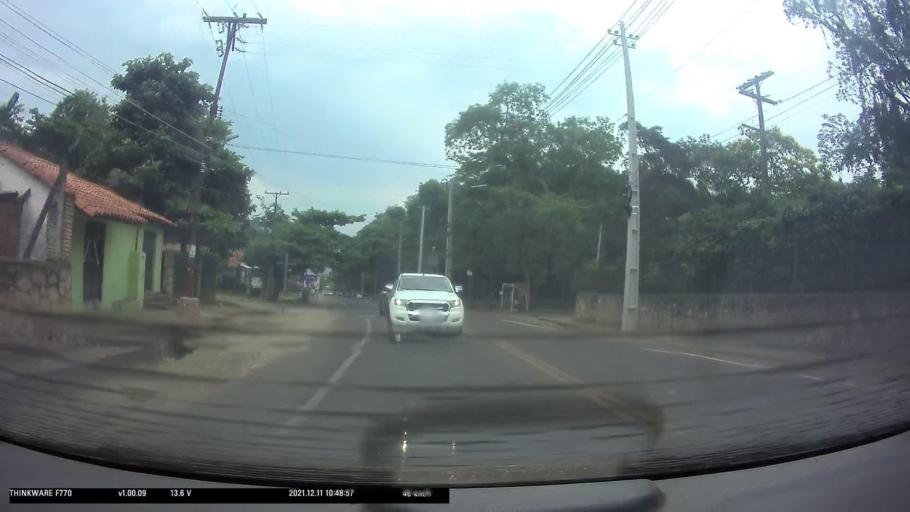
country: PY
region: Cordillera
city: San Bernardino
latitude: -25.2973
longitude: -57.2839
